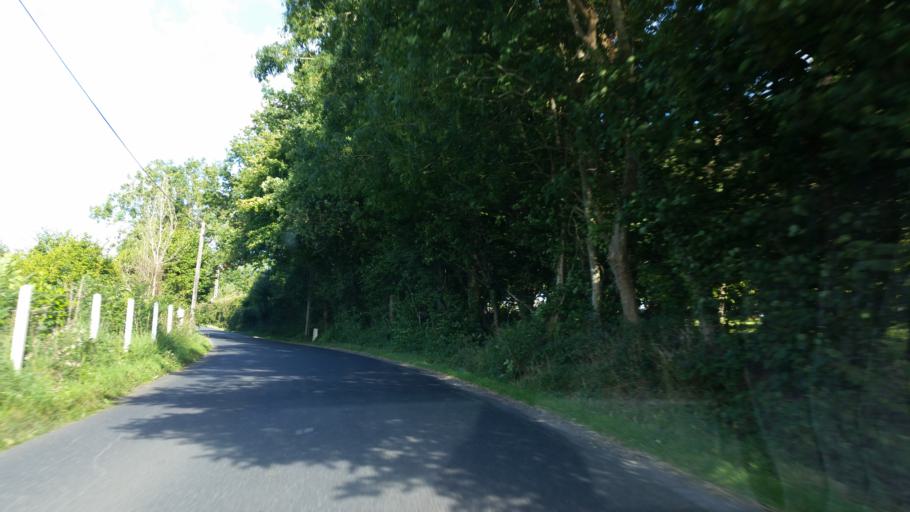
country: FR
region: Lower Normandy
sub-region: Departement du Calvados
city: Touques
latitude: 49.3379
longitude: 0.1294
